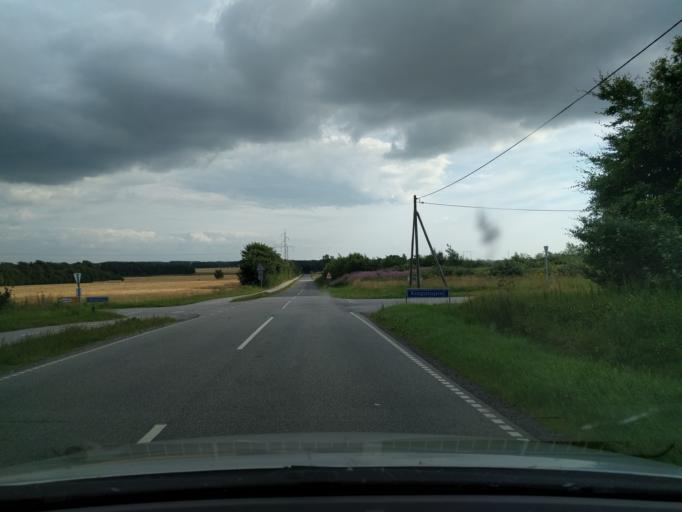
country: DK
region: Central Jutland
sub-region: Herning Kommune
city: Snejbjerg
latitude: 56.1114
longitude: 8.9079
